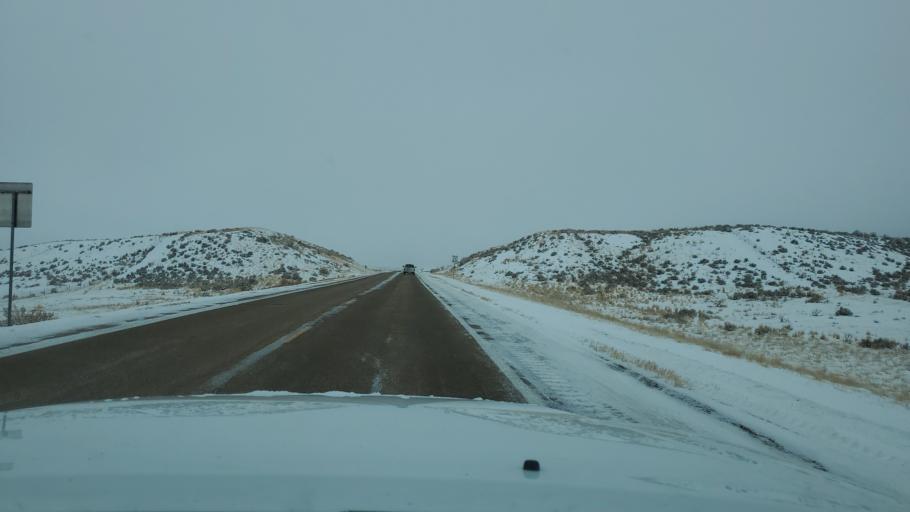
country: US
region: Colorado
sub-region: Rio Blanco County
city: Rangely
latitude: 40.2534
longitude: -108.6918
